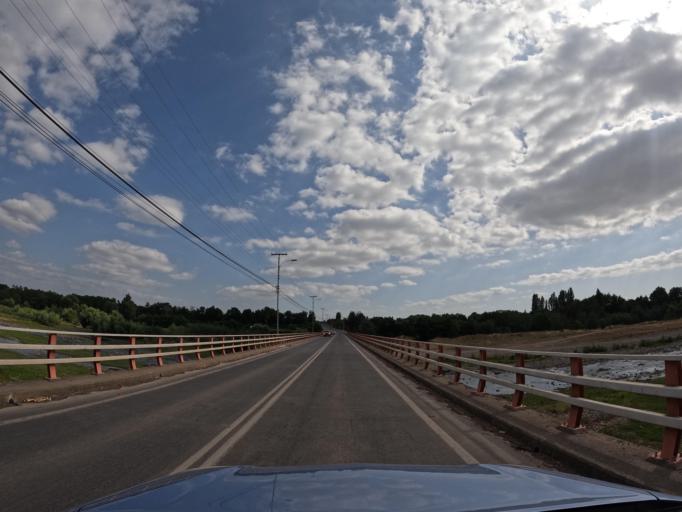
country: CL
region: Maule
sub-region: Provincia de Curico
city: Molina
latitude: -35.1540
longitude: -71.2839
